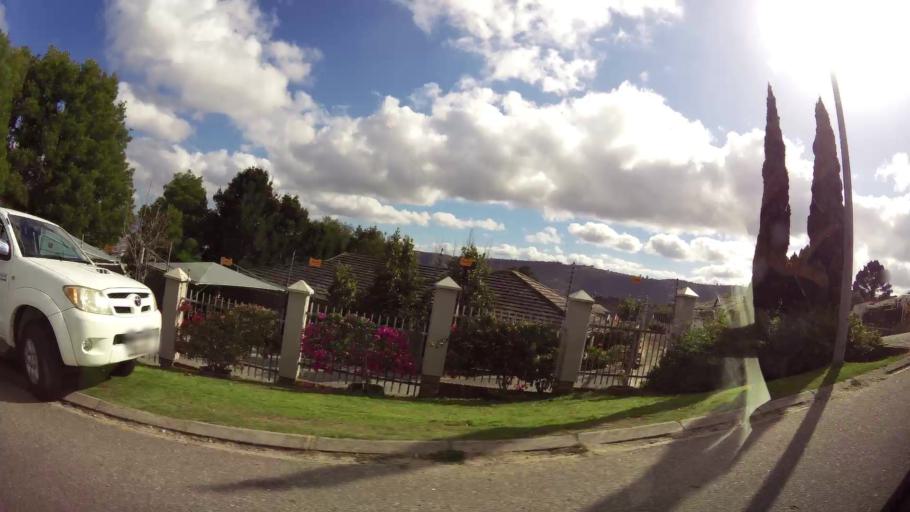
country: ZA
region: Western Cape
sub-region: Eden District Municipality
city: Knysna
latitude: -34.0522
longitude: 23.0792
